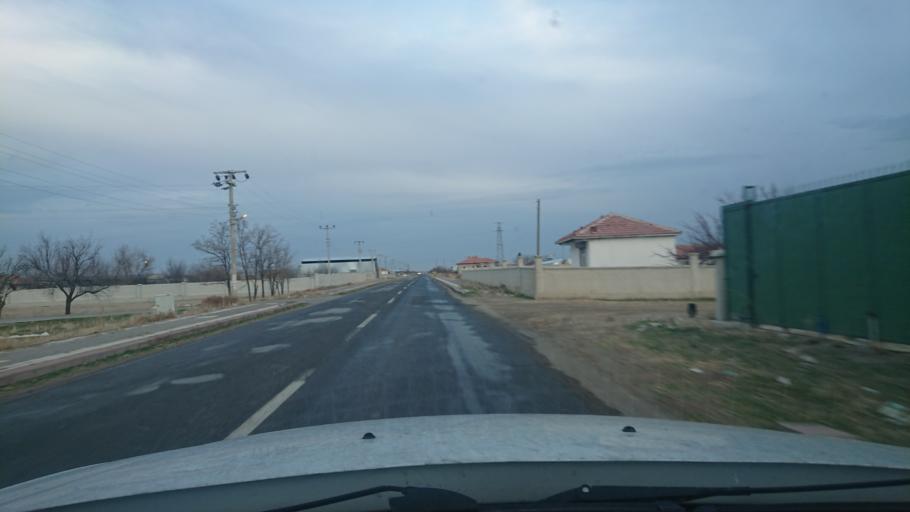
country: TR
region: Aksaray
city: Yesilova
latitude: 38.2946
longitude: 33.7592
